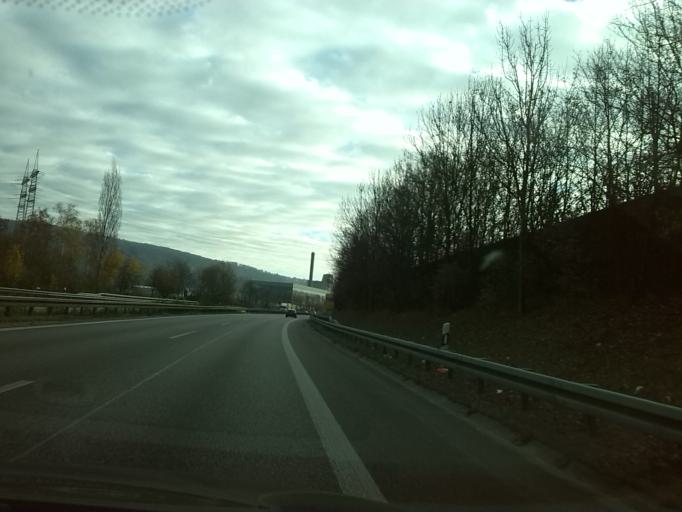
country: DE
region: Baden-Wuerttemberg
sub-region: Regierungsbezirk Stuttgart
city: Deizisau
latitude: 48.7165
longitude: 9.3879
